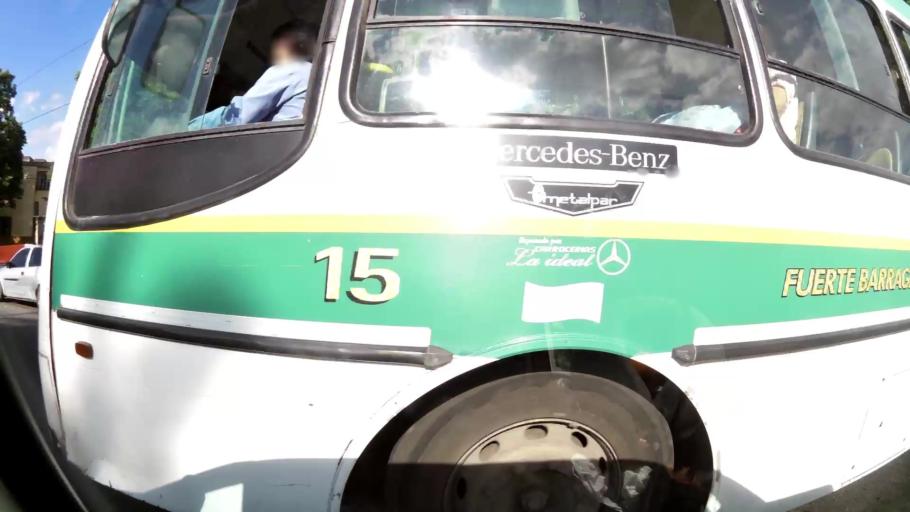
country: AR
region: Buenos Aires
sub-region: Partido de La Plata
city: La Plata
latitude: -34.9036
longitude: -57.9492
